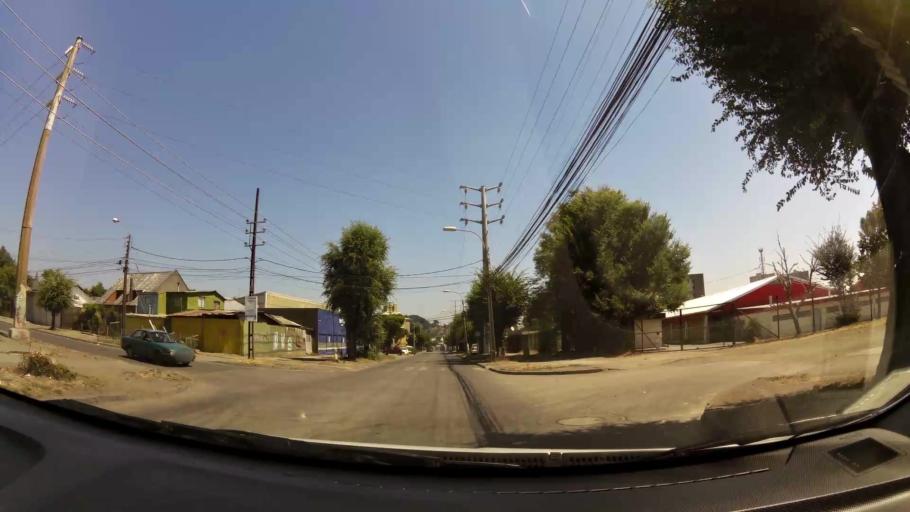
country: CL
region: Biobio
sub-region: Provincia de Concepcion
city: Concepcion
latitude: -36.8124
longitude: -73.0571
